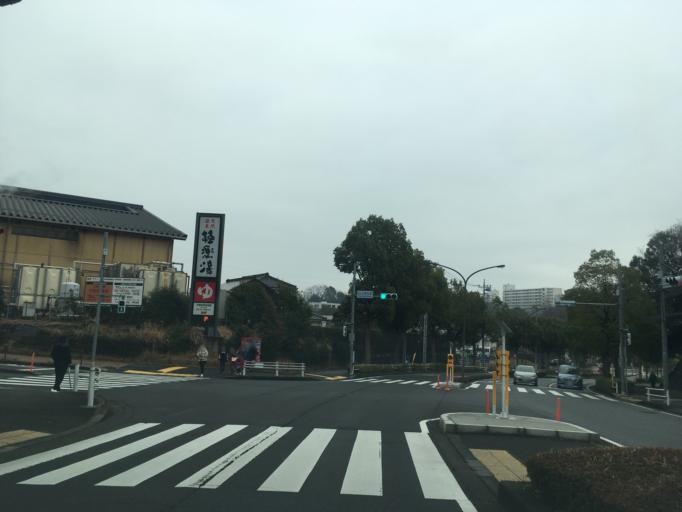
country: JP
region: Tokyo
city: Hino
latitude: 35.6229
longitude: 139.4282
